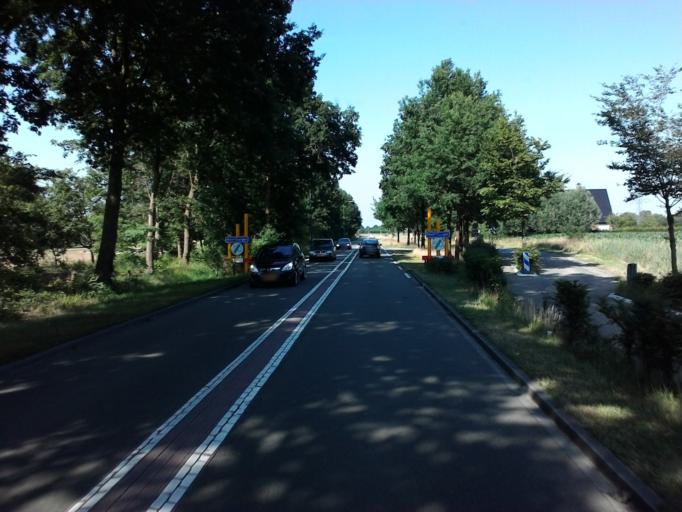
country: NL
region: Utrecht
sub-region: Gemeente Utrechtse Heuvelrug
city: Maarsbergen
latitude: 52.0619
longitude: 5.4054
